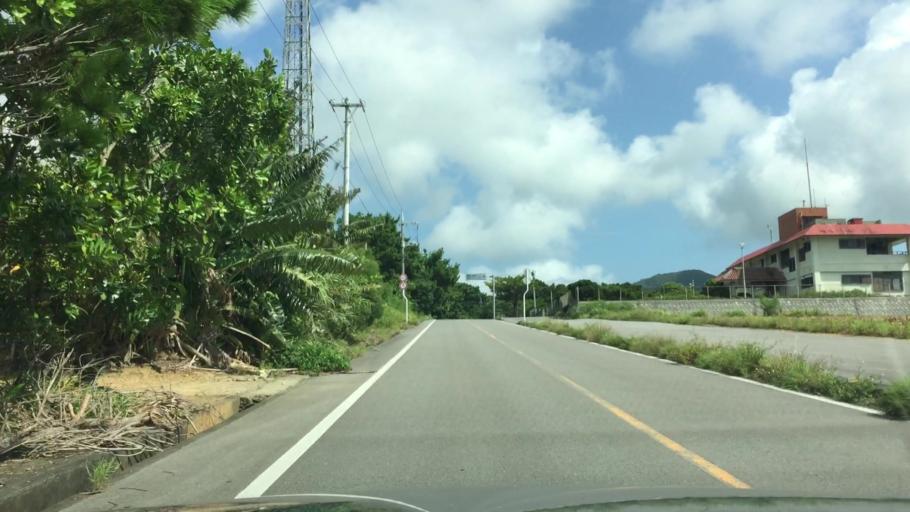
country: JP
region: Okinawa
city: Ishigaki
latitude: 24.4197
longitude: 124.2146
